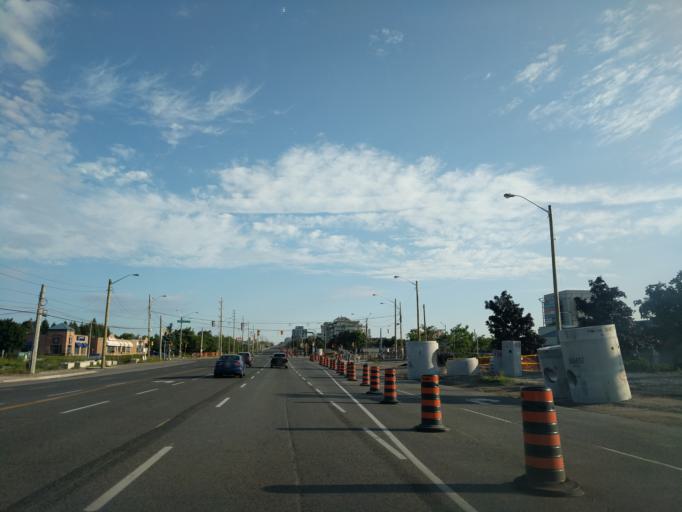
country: CA
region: Ontario
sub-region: York
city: Richmond Hill
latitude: 43.8938
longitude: -79.4425
